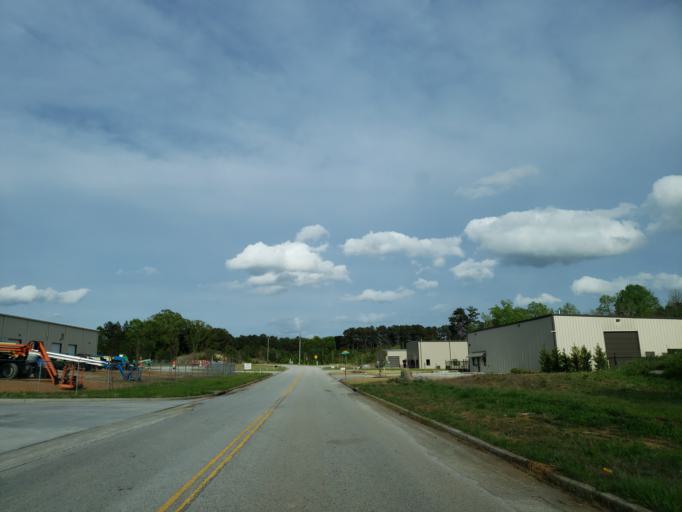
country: US
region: Georgia
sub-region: Paulding County
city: Hiram
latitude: 33.8776
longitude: -84.7430
